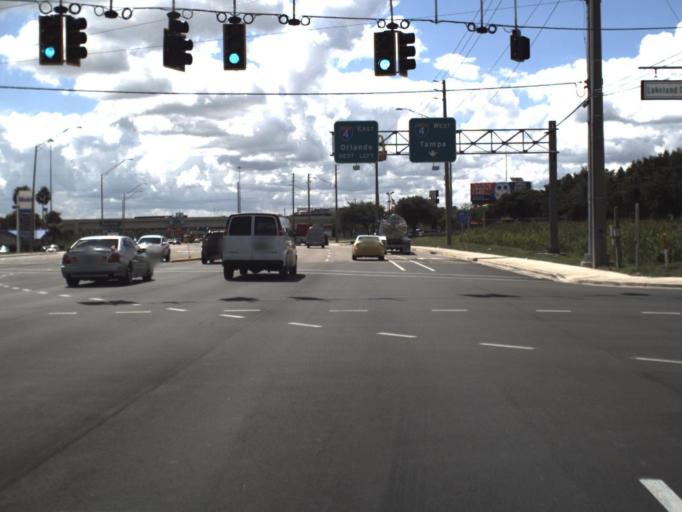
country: US
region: Florida
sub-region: Polk County
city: Gibsonia
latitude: 28.0881
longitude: -81.9729
